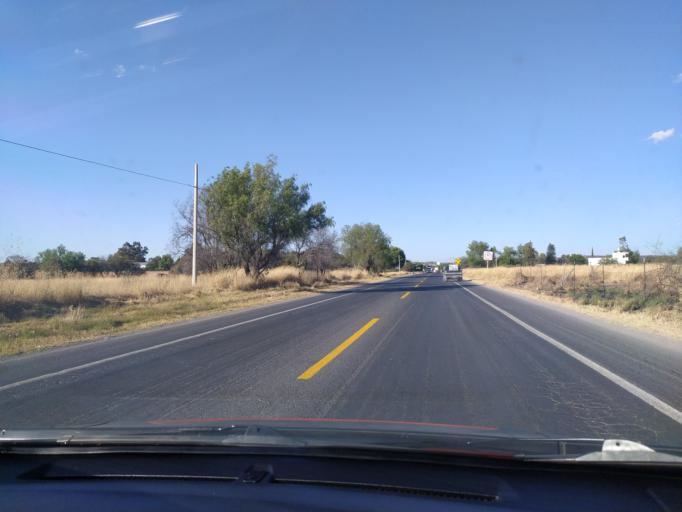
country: LA
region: Oudomxai
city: Muang La
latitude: 21.0177
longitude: 101.8271
